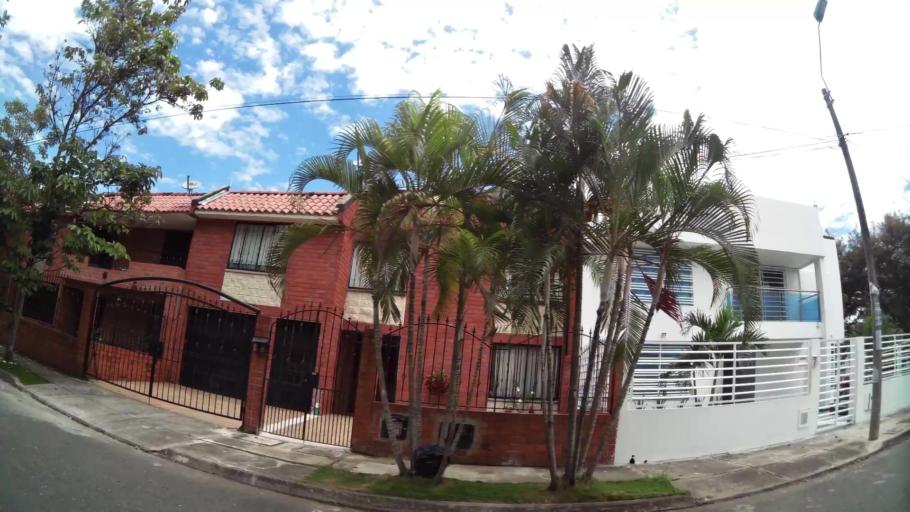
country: CO
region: Valle del Cauca
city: Cali
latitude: 3.3819
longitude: -76.5277
